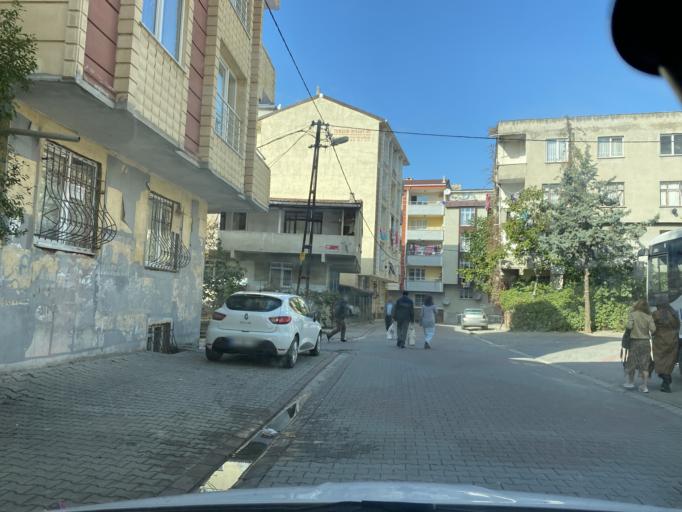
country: TR
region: Istanbul
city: Esenyurt
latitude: 41.0311
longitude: 28.6678
